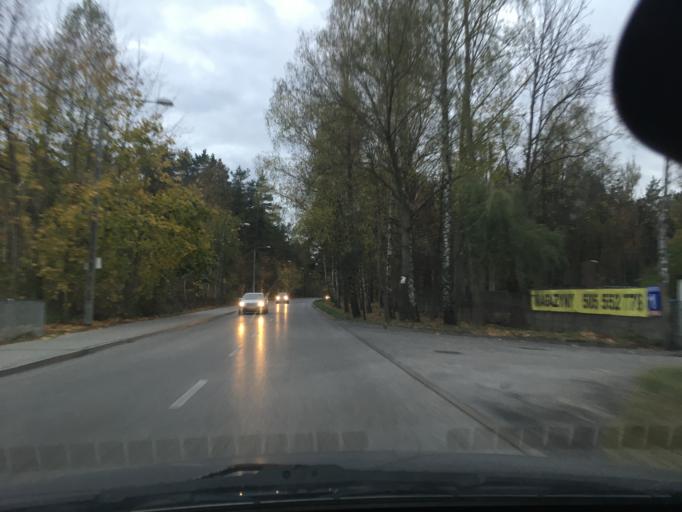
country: PL
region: Masovian Voivodeship
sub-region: Powiat piaseczynski
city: Lesznowola
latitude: 52.0823
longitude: 20.9393
